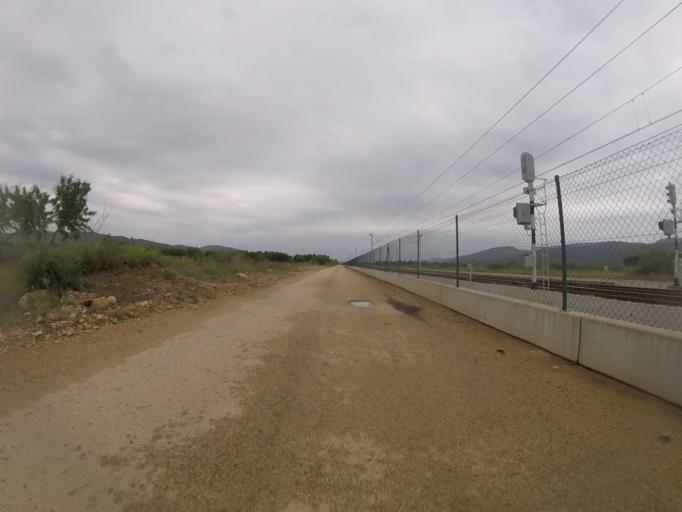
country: ES
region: Valencia
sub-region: Provincia de Castello
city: Alcala de Xivert
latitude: 40.3276
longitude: 0.2440
